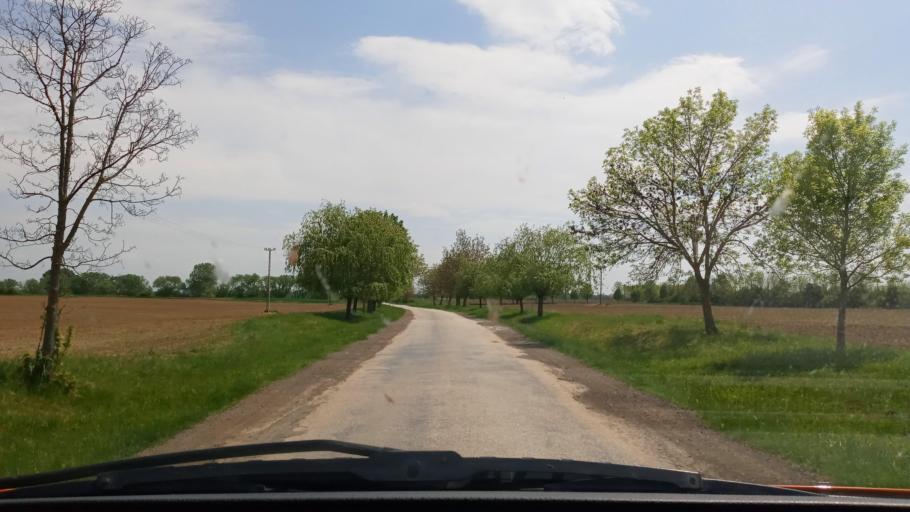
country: HU
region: Baranya
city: Villany
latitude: 45.8230
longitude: 18.5049
